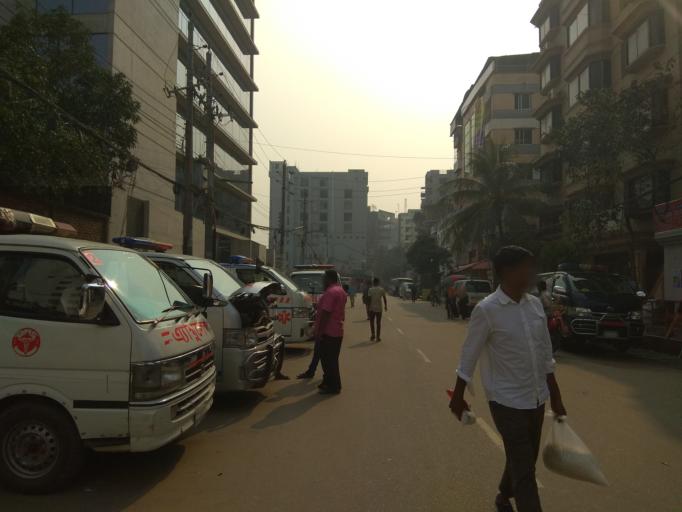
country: BD
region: Dhaka
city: Tungi
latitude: 23.8703
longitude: 90.3998
